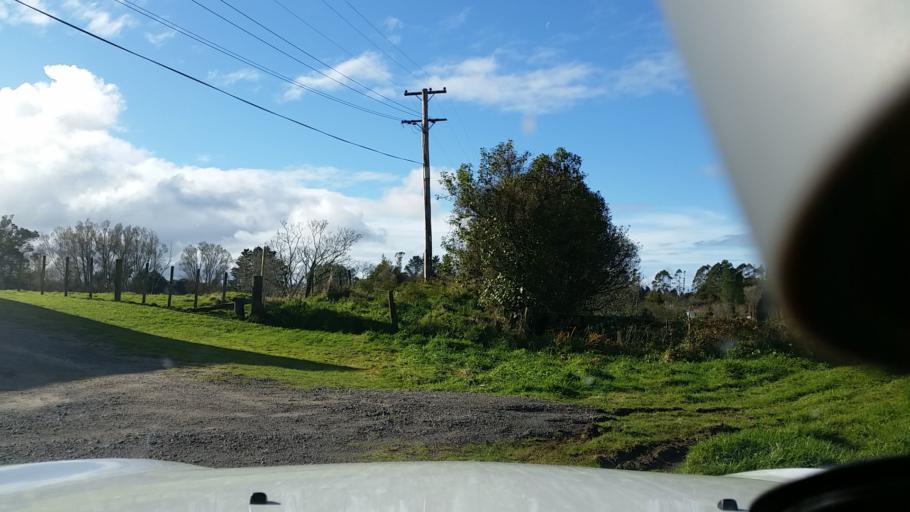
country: NZ
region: Bay of Plenty
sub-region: Rotorua District
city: Rotorua
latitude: -38.1005
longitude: 176.0813
